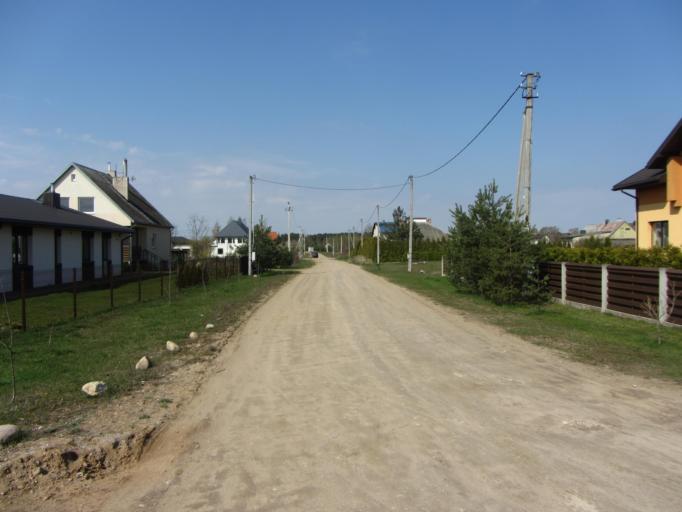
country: LT
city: Lentvaris
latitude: 54.6385
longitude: 25.0315
